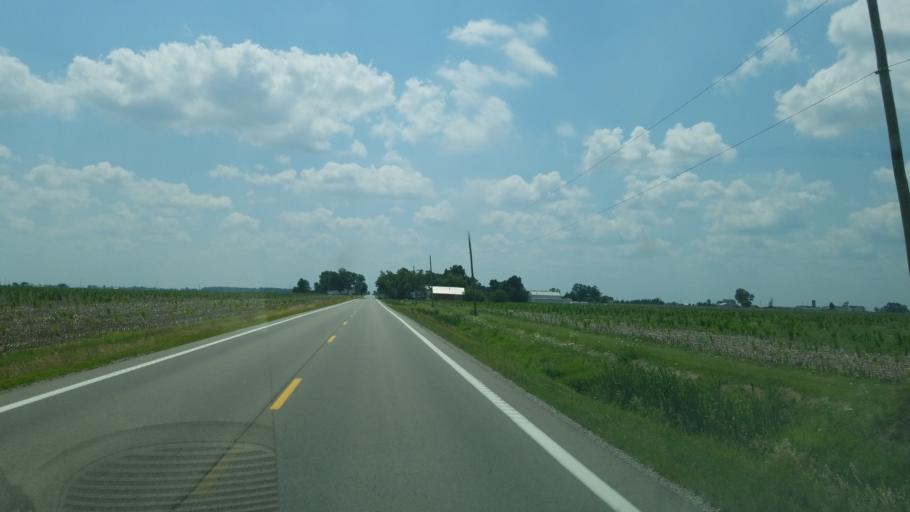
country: US
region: Ohio
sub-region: Henry County
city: Deshler
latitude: 41.3051
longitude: -83.9411
